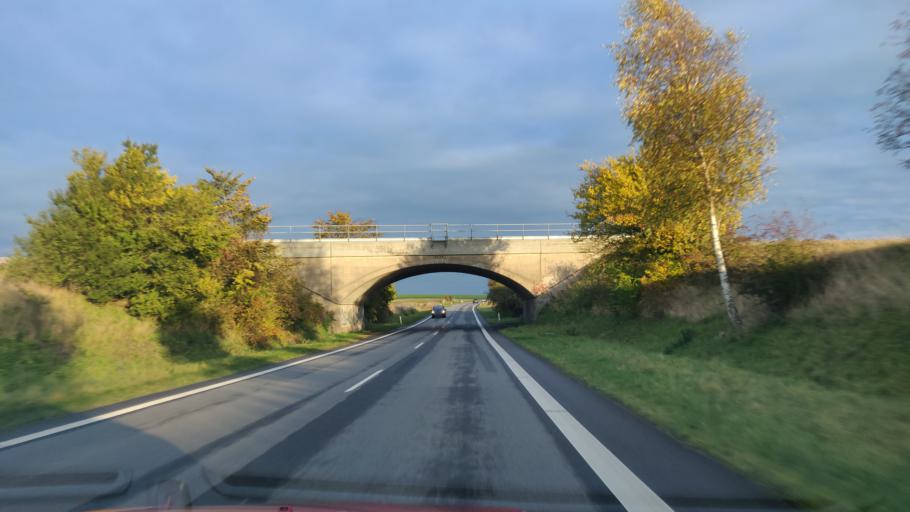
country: DK
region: Zealand
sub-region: Holbaek Kommune
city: Vipperod
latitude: 55.6838
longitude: 11.7250
